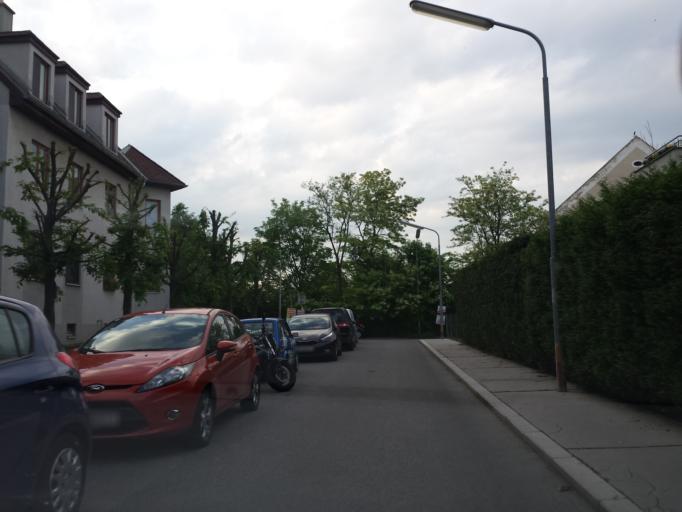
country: AT
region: Lower Austria
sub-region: Politischer Bezirk Ganserndorf
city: Gross-Enzersdorf
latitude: 48.2155
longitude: 16.5235
